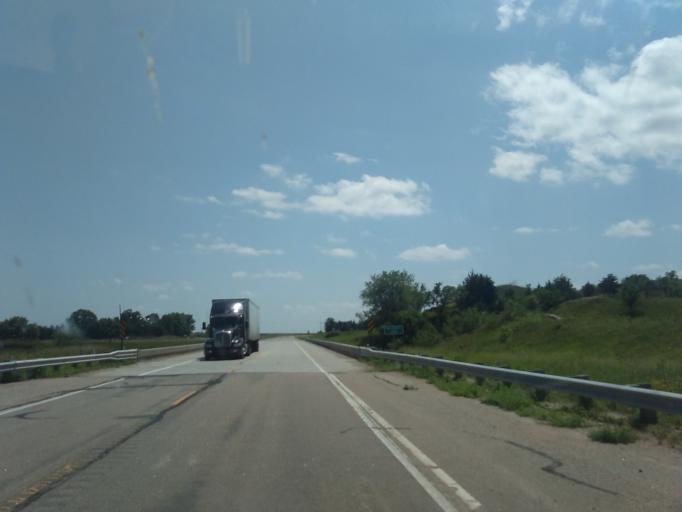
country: US
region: Nebraska
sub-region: Dawson County
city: Lexington
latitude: 40.6940
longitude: -99.7945
